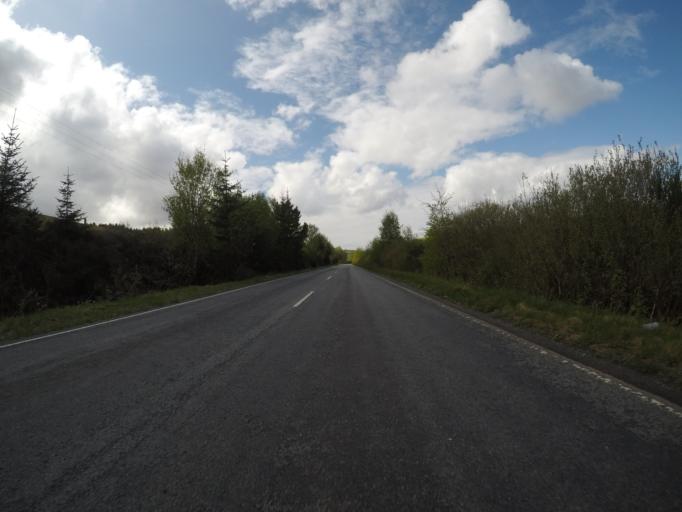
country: GB
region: Scotland
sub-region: Highland
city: Isle of Skye
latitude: 57.4523
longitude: -6.3099
